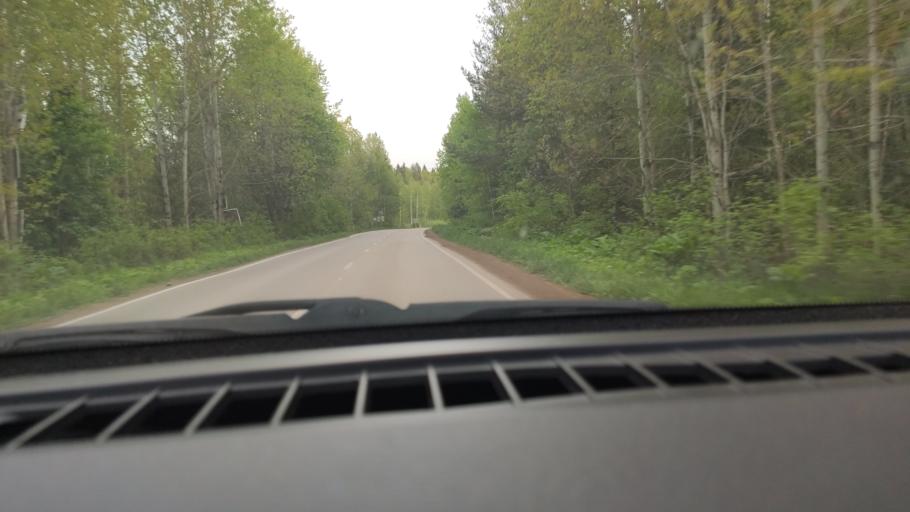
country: RU
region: Perm
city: Overyata
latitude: 58.0783
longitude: 56.0020
